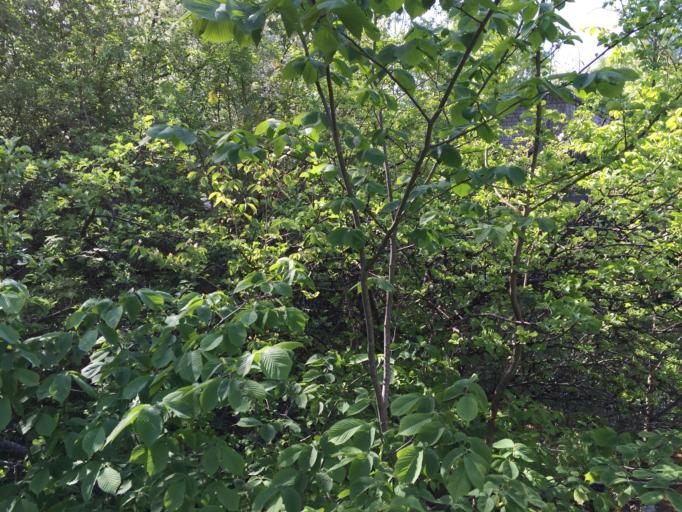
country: LV
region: Bauskas Rajons
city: Bauska
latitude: 56.4148
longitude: 24.1899
